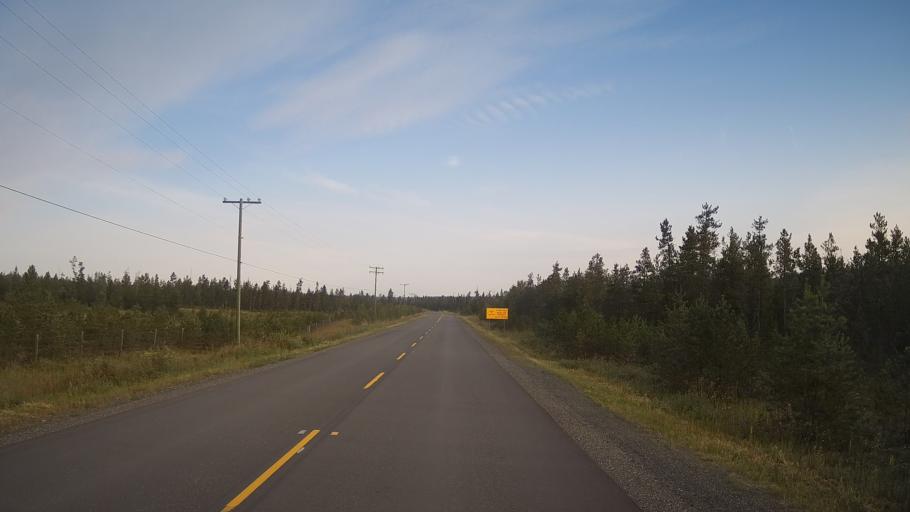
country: CA
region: British Columbia
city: Hanceville
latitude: 52.1326
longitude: -123.6989
